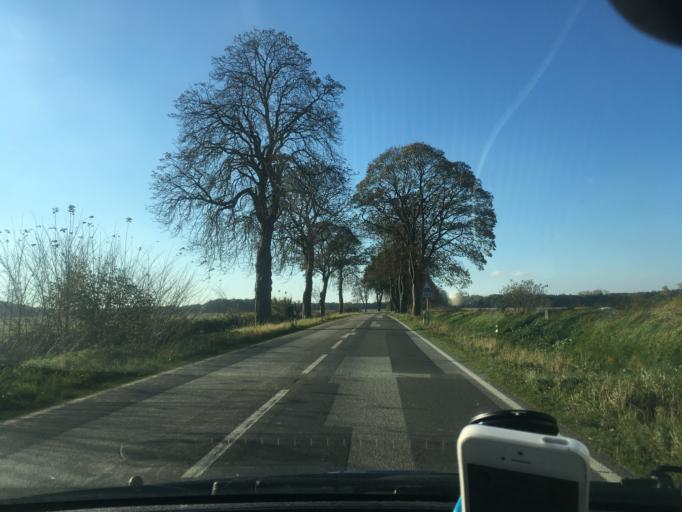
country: DE
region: Mecklenburg-Vorpommern
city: Wittenburg
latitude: 53.5207
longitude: 11.0007
